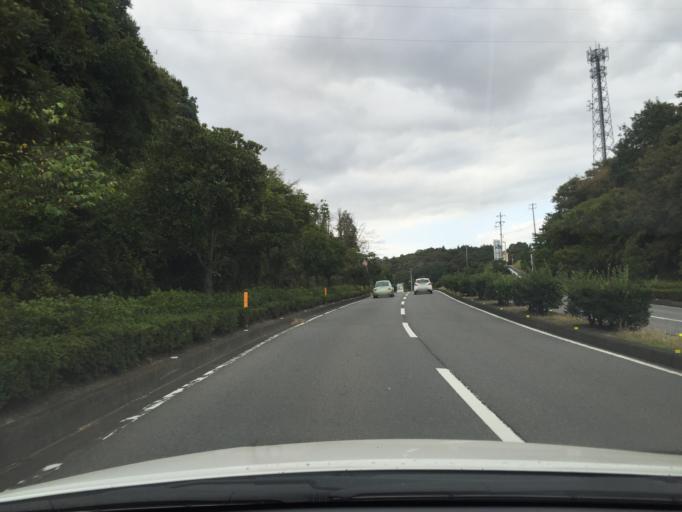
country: JP
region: Ibaraki
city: Kitaibaraki
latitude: 36.9003
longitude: 140.7589
